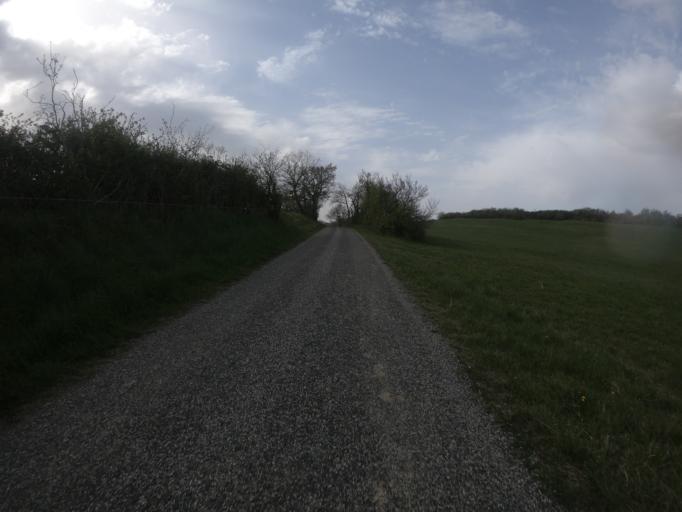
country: FR
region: Languedoc-Roussillon
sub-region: Departement de l'Aude
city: Belpech
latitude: 43.1308
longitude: 1.7593
